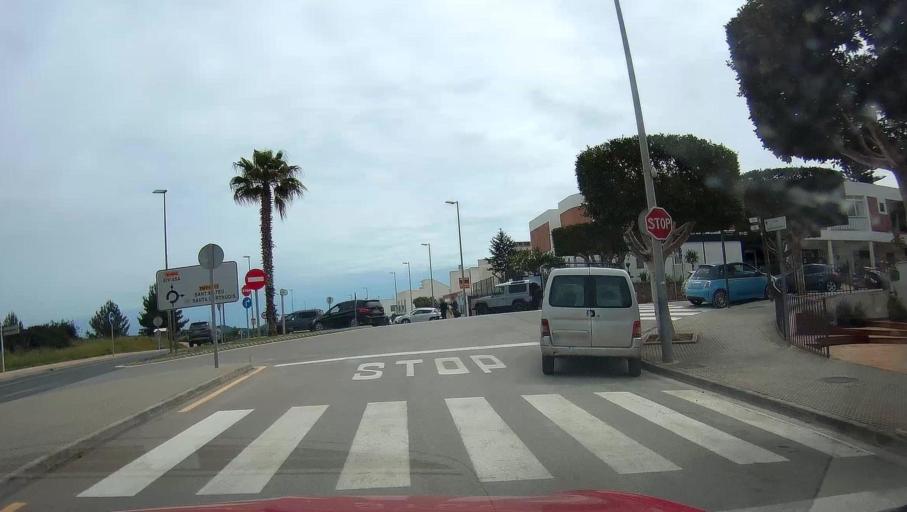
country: ES
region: Balearic Islands
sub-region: Illes Balears
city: Ibiza
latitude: 38.9979
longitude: 1.4303
